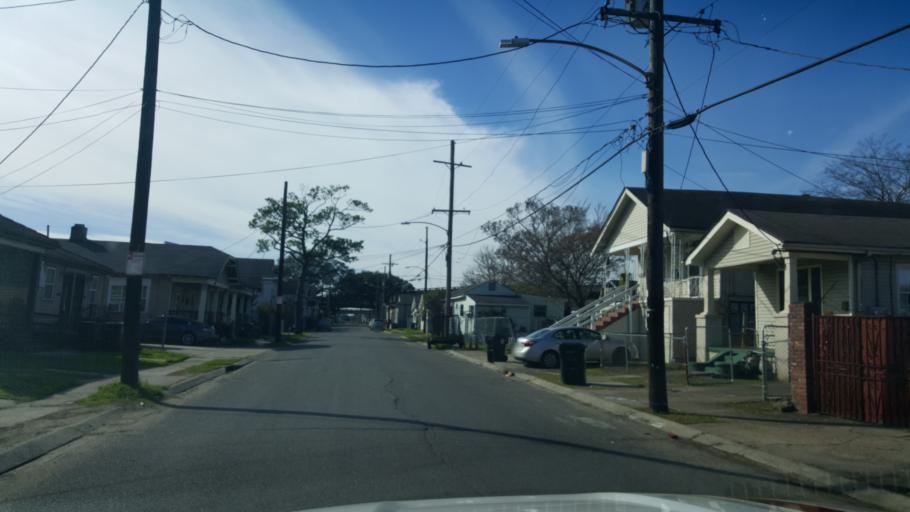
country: US
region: Louisiana
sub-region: Orleans Parish
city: New Orleans
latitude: 29.9798
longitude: -90.0555
